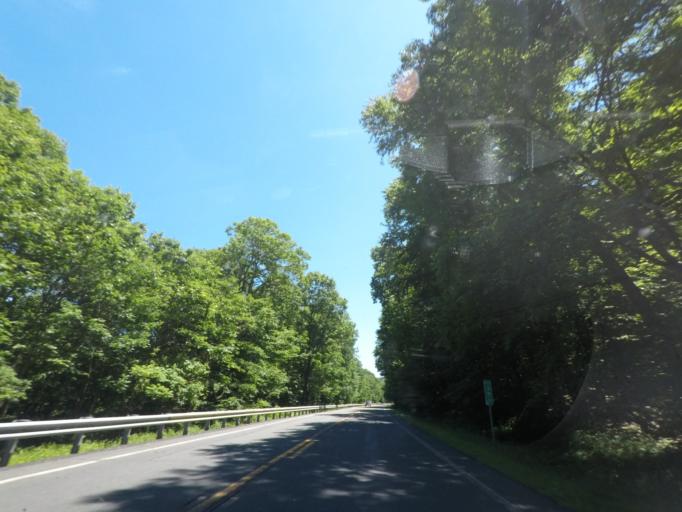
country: US
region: Massachusetts
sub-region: Hampshire County
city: Westhampton
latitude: 42.2460
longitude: -72.9197
